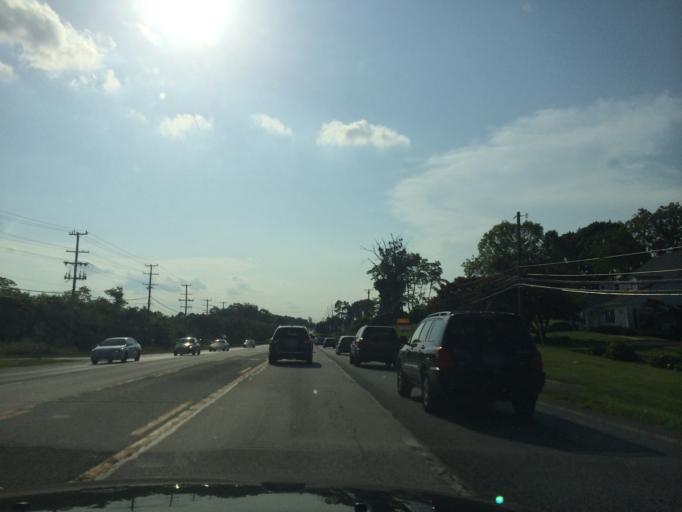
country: US
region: Maryland
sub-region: Carroll County
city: Eldersburg
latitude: 39.4002
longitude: -76.9370
